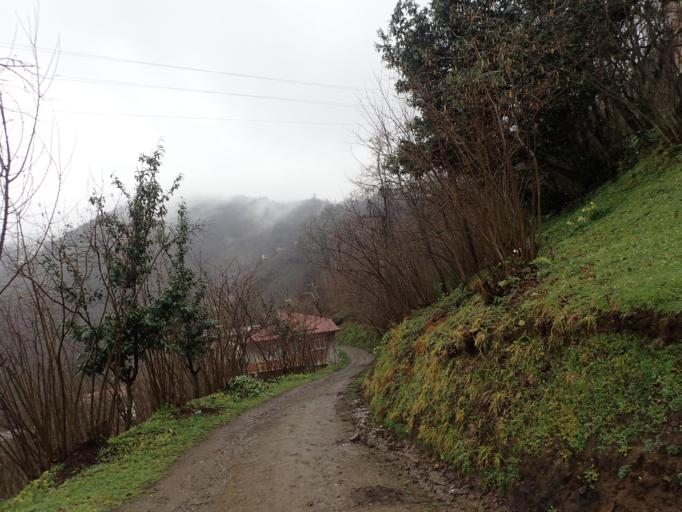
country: TR
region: Ordu
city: Camas
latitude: 40.9135
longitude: 37.5719
